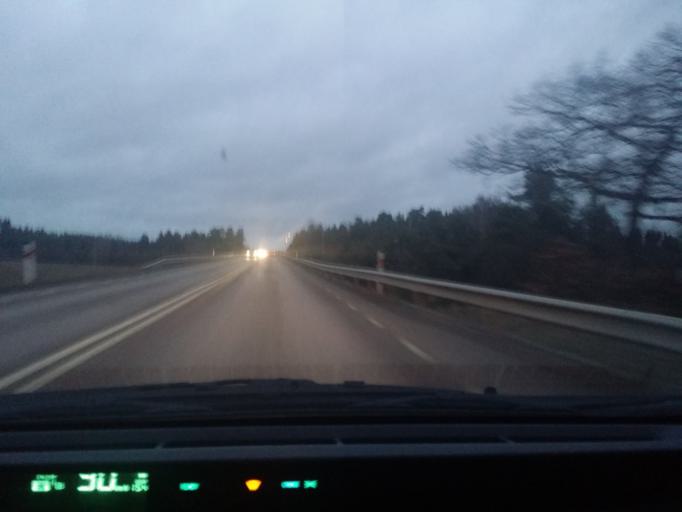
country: SE
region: Vaestmanland
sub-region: Hallstahammars Kommun
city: Kolback
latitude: 59.5621
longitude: 16.3464
